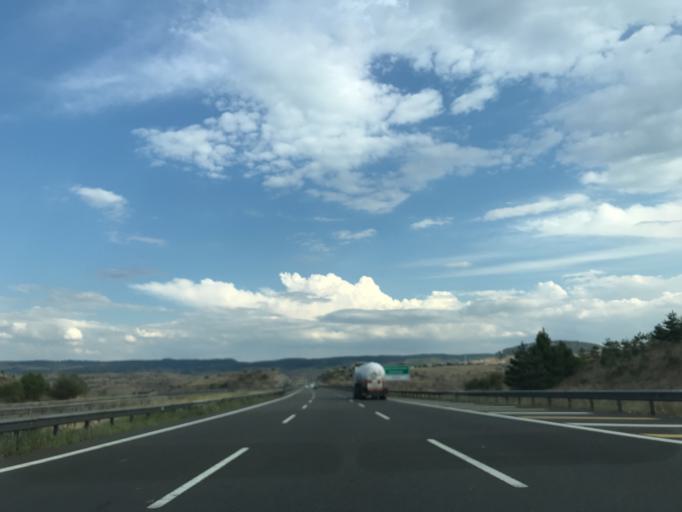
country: TR
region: Bolu
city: Gerede
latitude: 40.6783
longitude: 32.2244
